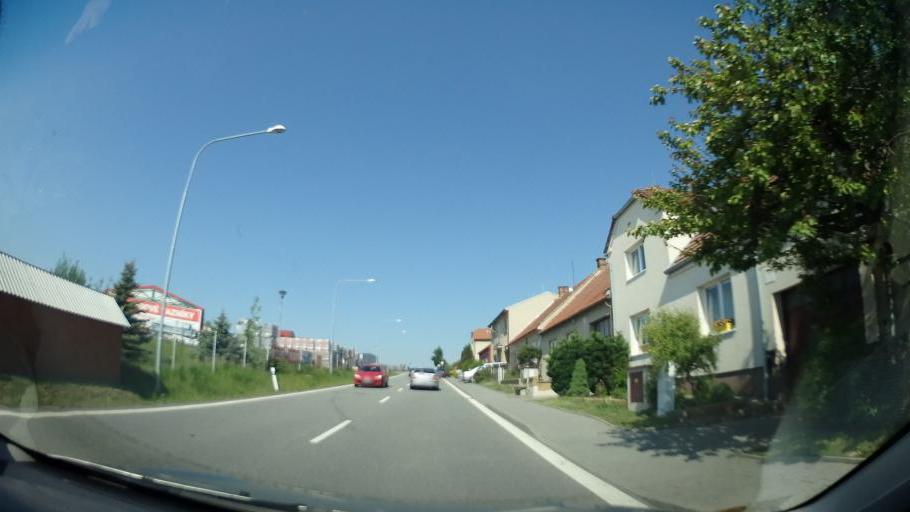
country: CZ
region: South Moravian
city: Zbraslav
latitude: 49.1839
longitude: 16.2795
